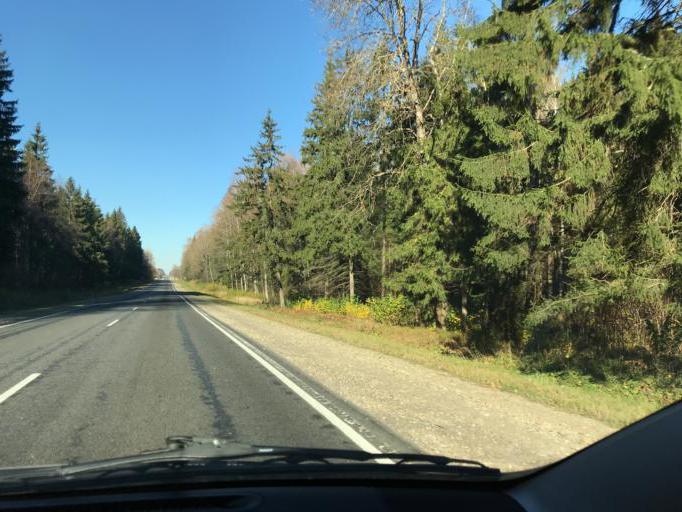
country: BY
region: Vitebsk
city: Polatsk
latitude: 55.5245
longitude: 28.7291
